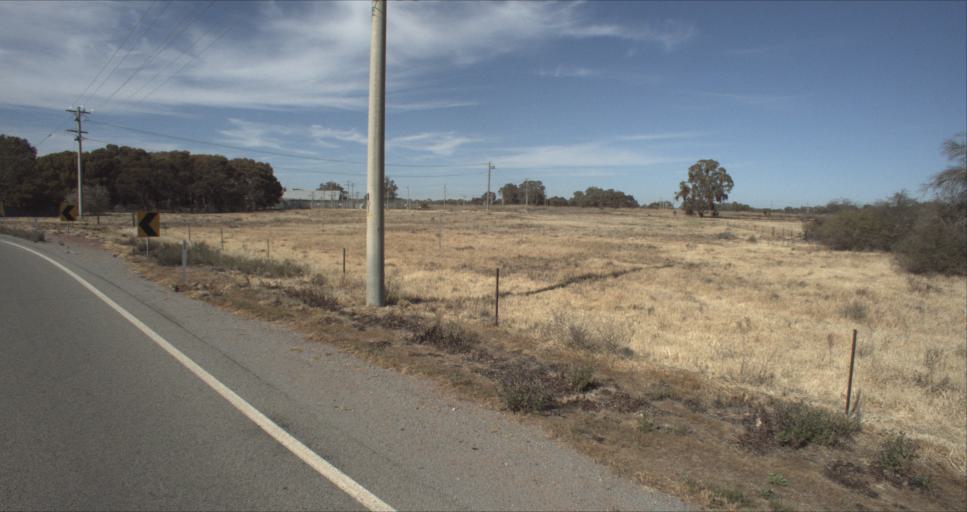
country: AU
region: New South Wales
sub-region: Leeton
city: Leeton
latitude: -34.6014
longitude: 146.4063
